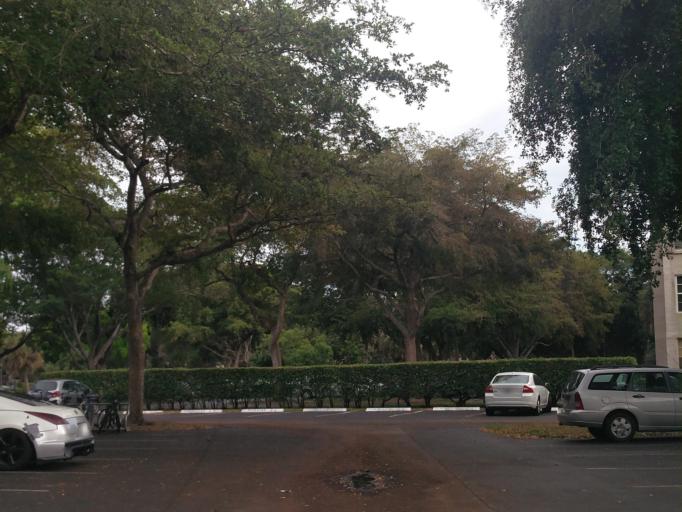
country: US
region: Florida
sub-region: Broward County
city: Pine Island Ridge
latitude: 26.0990
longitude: -80.2743
